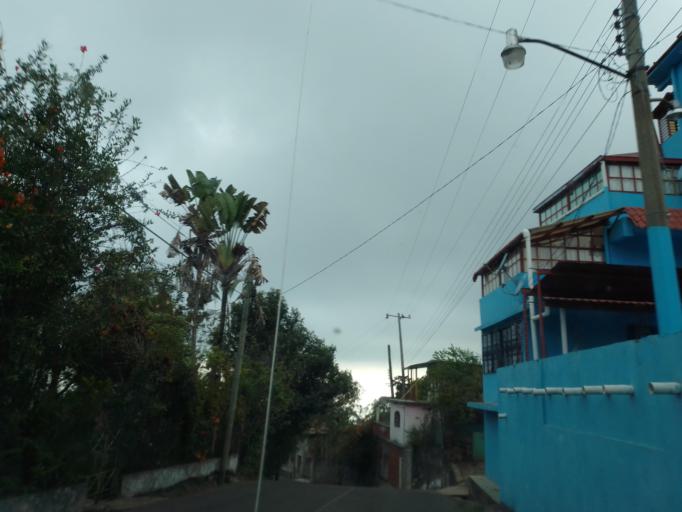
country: MX
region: Chiapas
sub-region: Union Juarez
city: Santo Domingo
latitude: 15.0707
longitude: -92.0818
